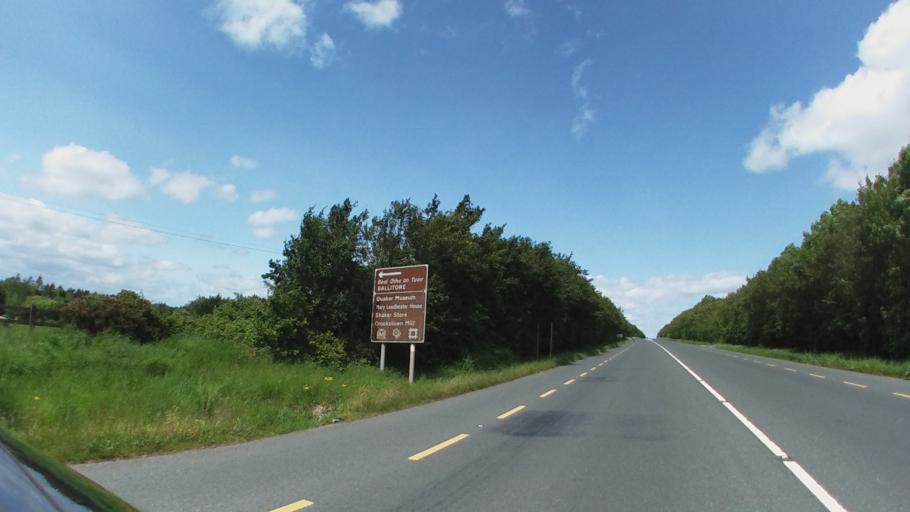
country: IE
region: Leinster
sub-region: Kildare
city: Moone
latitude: 53.0048
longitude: -6.8047
